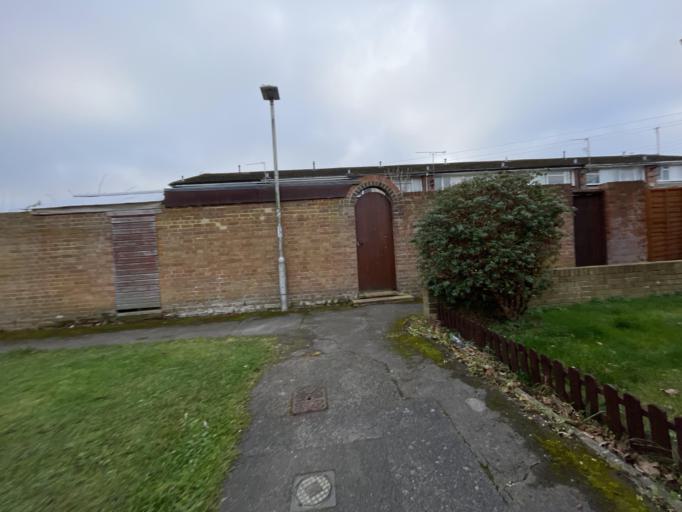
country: GB
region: England
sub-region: West Berkshire
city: Tilehurst
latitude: 51.4542
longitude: -1.0212
